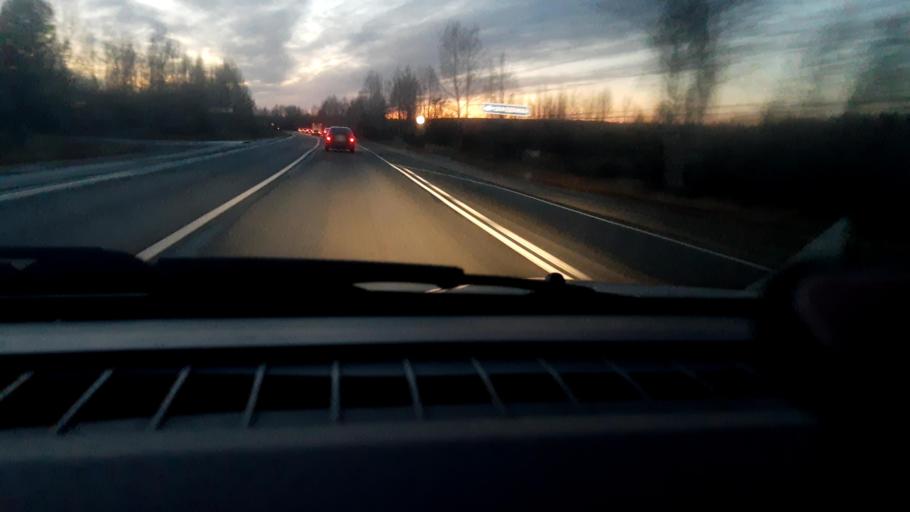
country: RU
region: Nizjnij Novgorod
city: Sukhobezvodnoye
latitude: 56.8612
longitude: 44.8536
